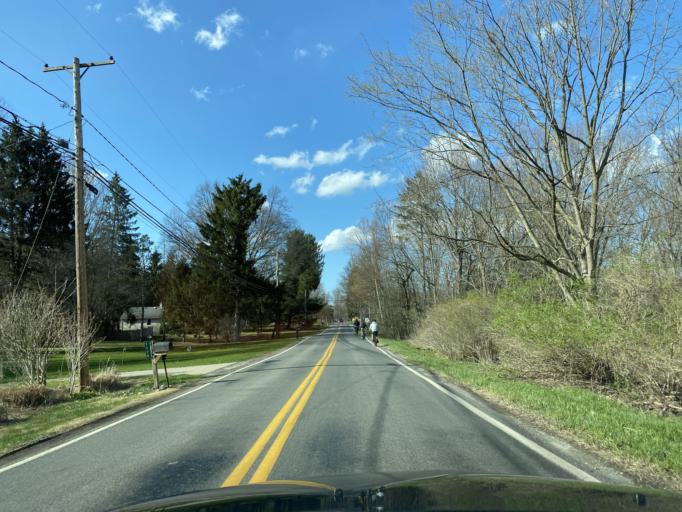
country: US
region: Ohio
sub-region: Summit County
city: Fairlawn
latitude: 41.0921
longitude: -81.6041
